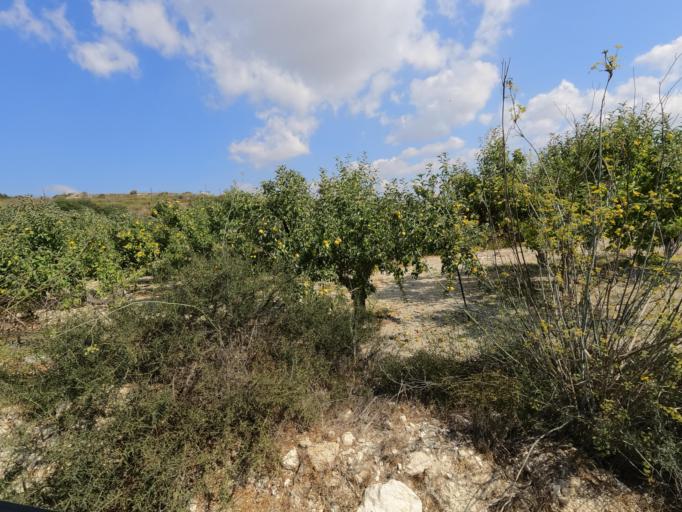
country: CY
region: Pafos
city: Mesogi
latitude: 34.8733
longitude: 32.4919
